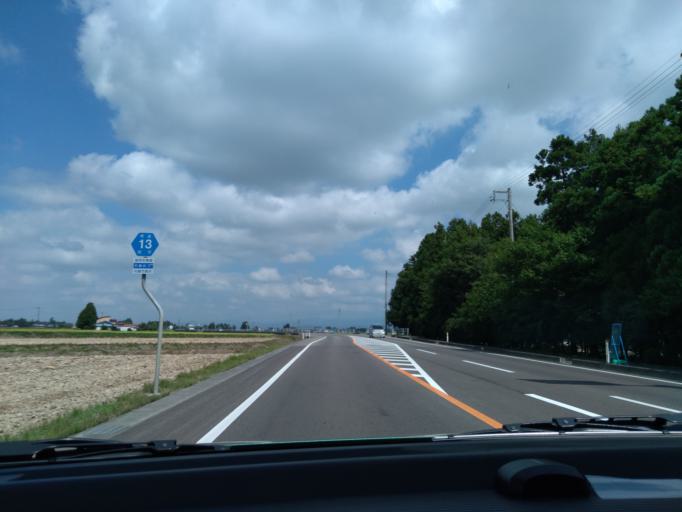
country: JP
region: Iwate
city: Hanamaki
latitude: 39.4354
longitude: 141.0951
